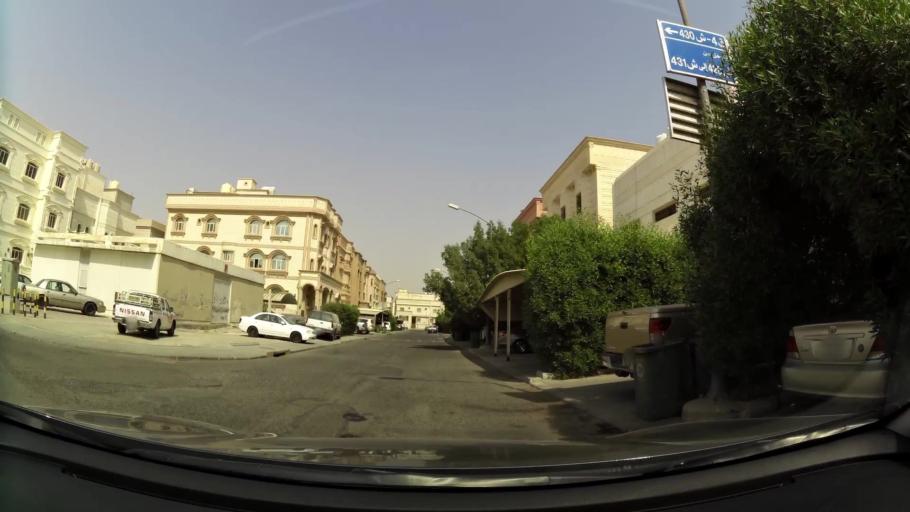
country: KW
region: Muhafazat al Jahra'
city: Al Jahra'
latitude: 29.3010
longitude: 47.7165
